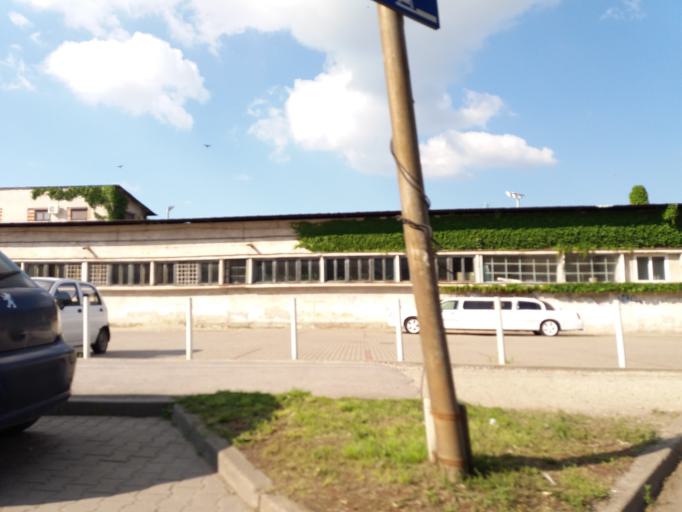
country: RO
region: Arad
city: Arad
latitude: 46.1846
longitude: 21.3189
